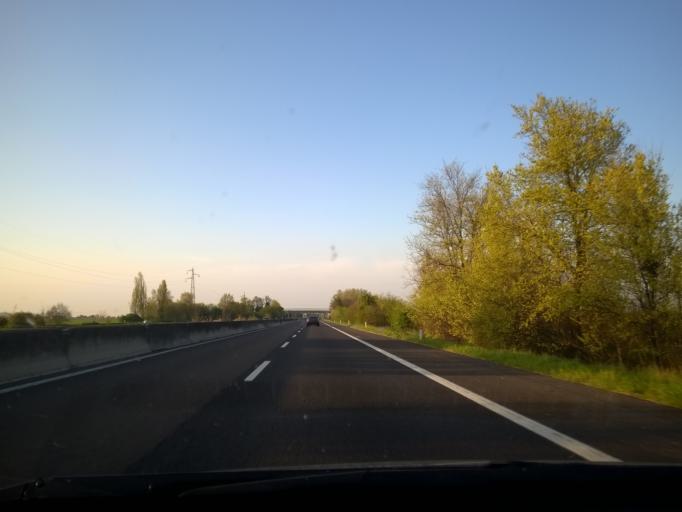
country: IT
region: Emilia-Romagna
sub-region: Provincia di Ferrara
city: Porotto-Cassama
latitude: 44.8116
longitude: 11.5545
